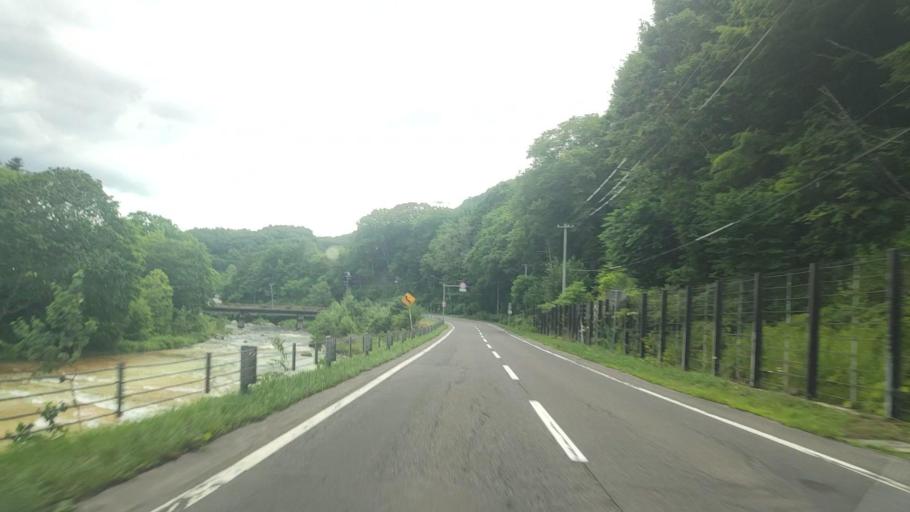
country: JP
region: Hokkaido
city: Date
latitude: 42.6248
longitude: 141.0246
